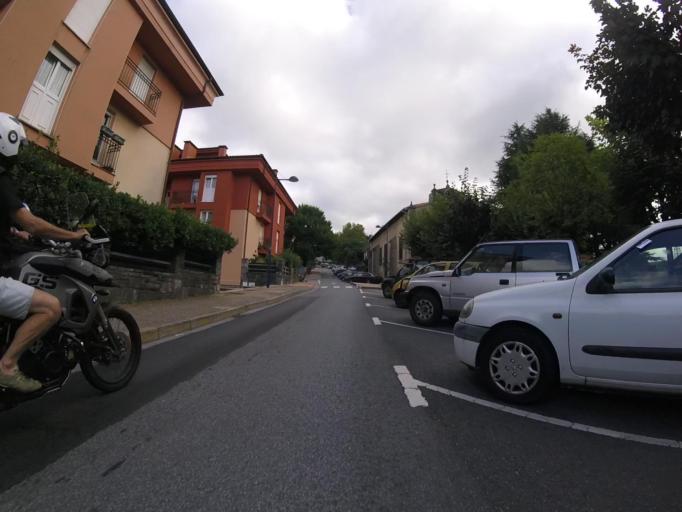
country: ES
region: Basque Country
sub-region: Provincia de Guipuzcoa
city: Errenteria
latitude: 43.3082
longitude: -1.8957
